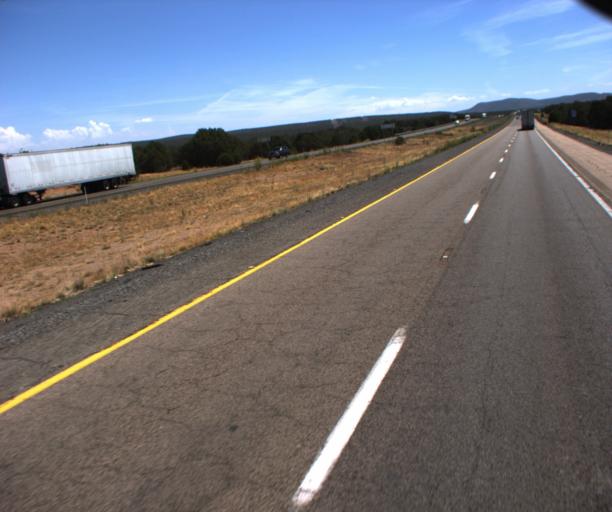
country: US
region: Arizona
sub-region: Mohave County
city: Peach Springs
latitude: 35.1908
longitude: -113.3565
